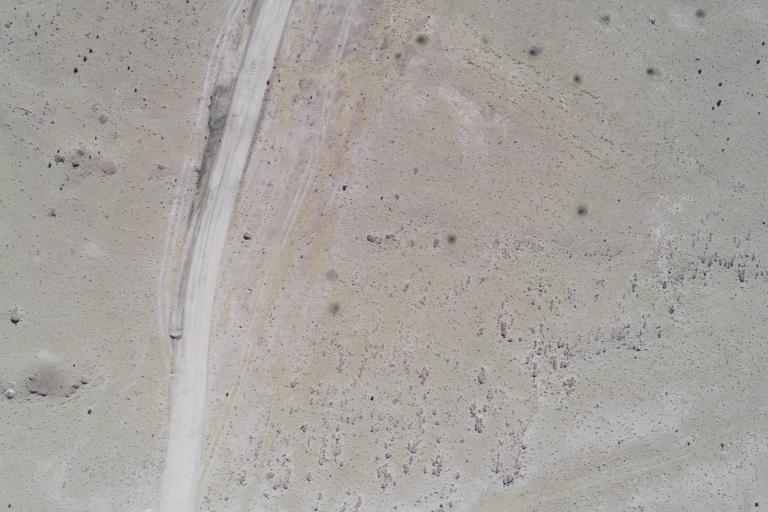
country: BO
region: Potosi
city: Colchani
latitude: -20.3523
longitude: -66.9010
